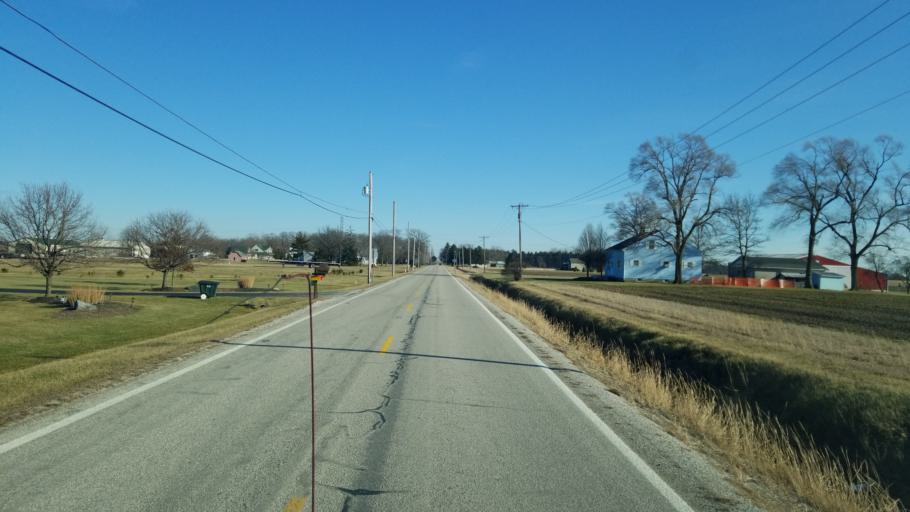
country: US
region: Ohio
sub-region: Wood County
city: Luckey
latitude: 41.4500
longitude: -83.4528
